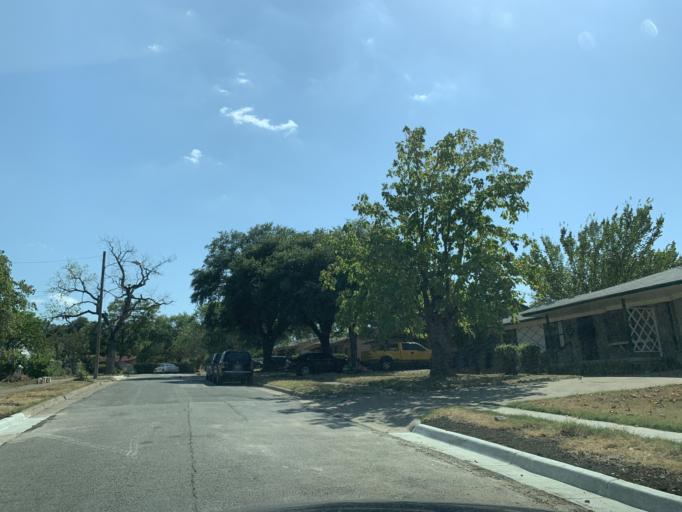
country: US
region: Texas
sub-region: Dallas County
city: Hutchins
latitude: 32.6775
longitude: -96.7959
